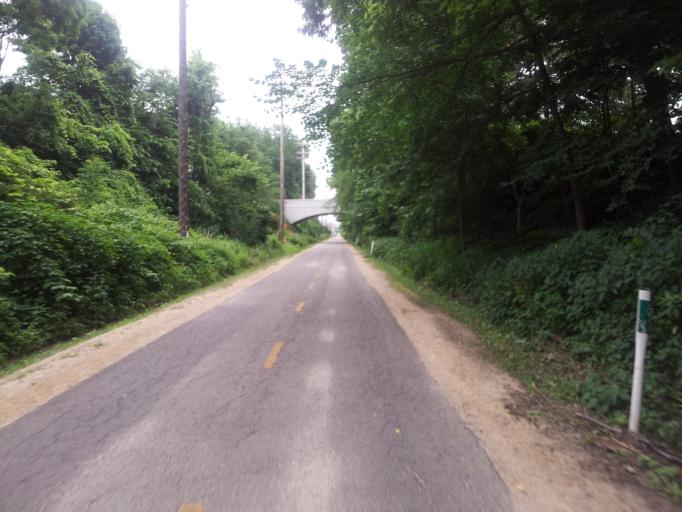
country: US
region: Wisconsin
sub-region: Dane County
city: Madison
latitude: 43.0665
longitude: -89.4180
